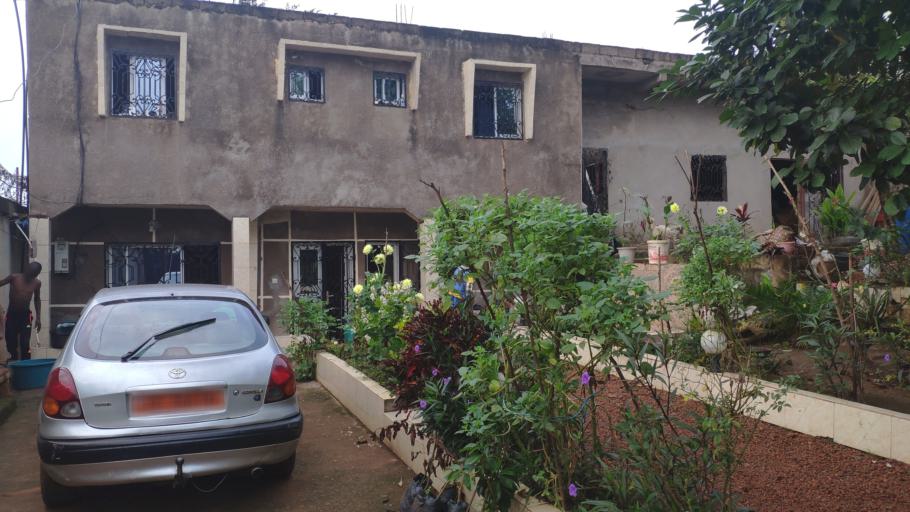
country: CM
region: Centre
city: Yaounde
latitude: 3.8155
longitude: 11.5242
